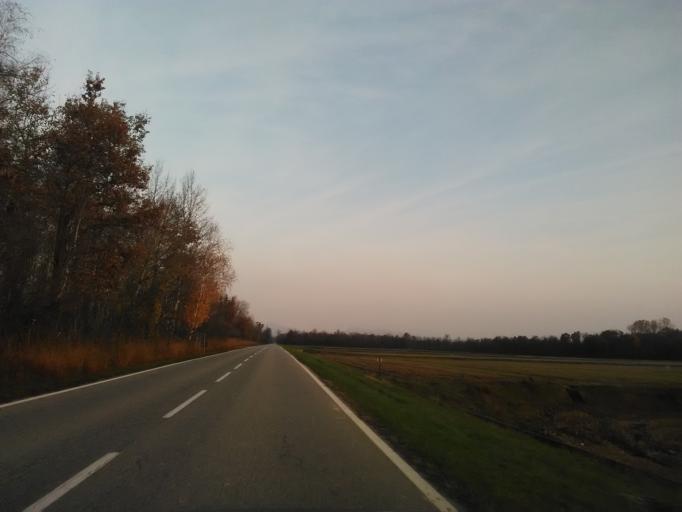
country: IT
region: Piedmont
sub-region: Provincia di Vercelli
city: Rovasenda
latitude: 45.5588
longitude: 8.2980
